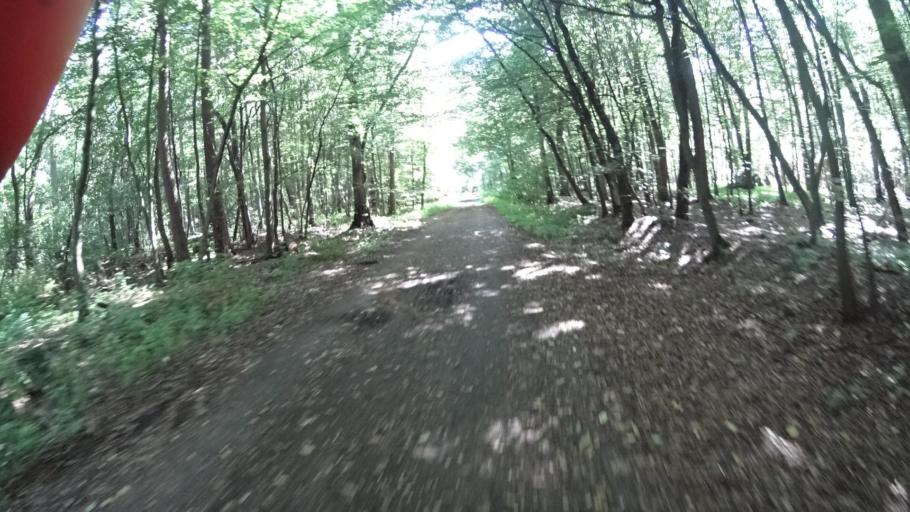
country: PL
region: Masovian Voivodeship
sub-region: Powiat piaseczynski
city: Jozefoslaw
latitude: 52.1153
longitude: 21.0552
